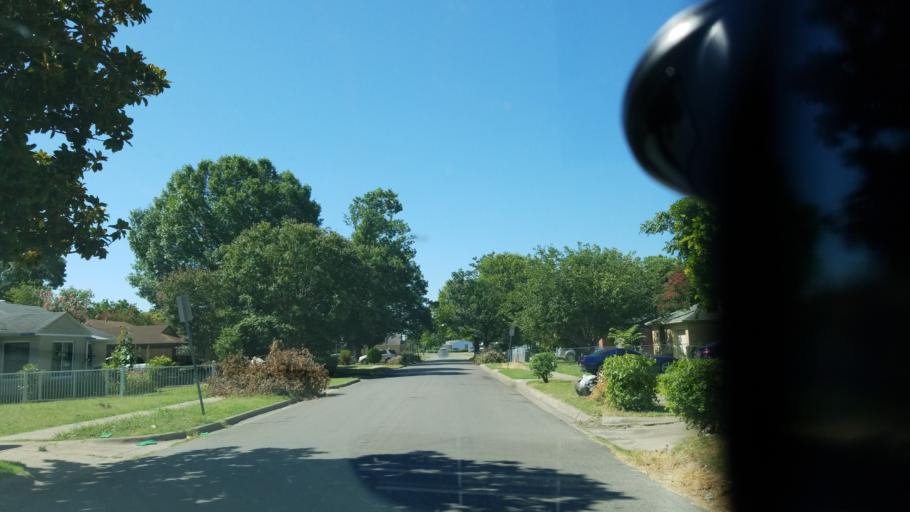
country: US
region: Texas
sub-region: Dallas County
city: Cockrell Hill
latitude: 32.6999
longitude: -96.8134
